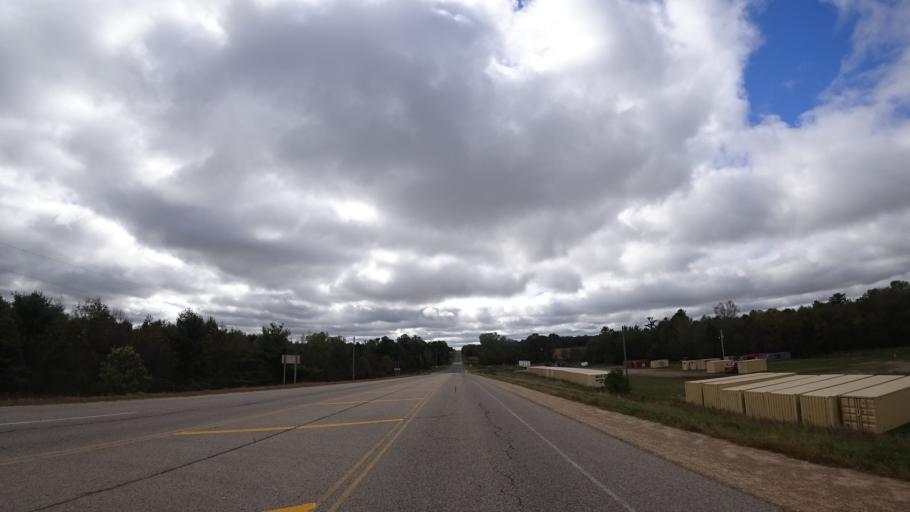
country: US
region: Wisconsin
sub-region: Saint Croix County
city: Woodville
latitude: 44.9334
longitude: -92.2782
